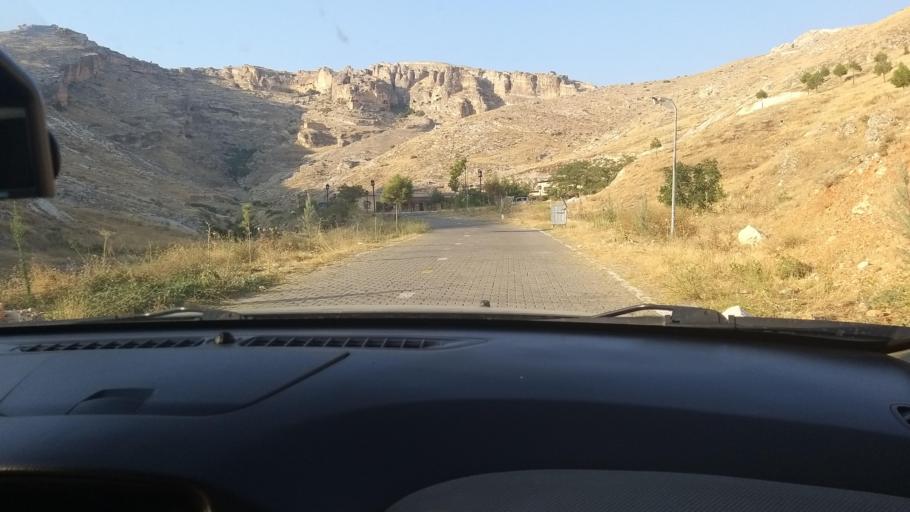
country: TR
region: Diyarbakir
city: Silvan
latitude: 38.1301
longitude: 41.0881
